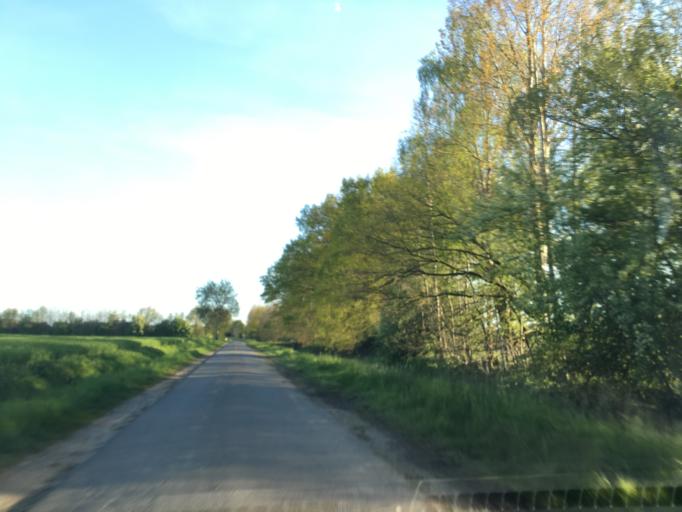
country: DE
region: North Rhine-Westphalia
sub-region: Regierungsbezirk Munster
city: Muenster
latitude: 52.0176
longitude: 7.6119
